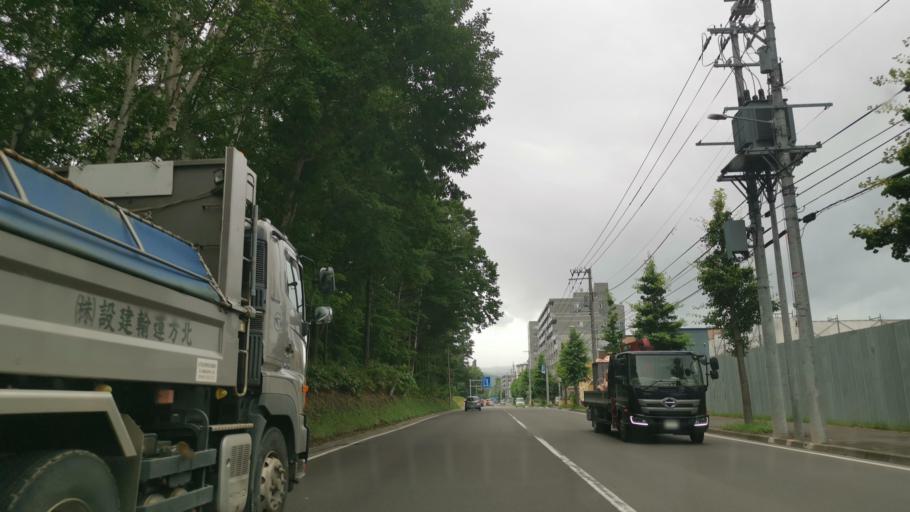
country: JP
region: Hokkaido
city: Sapporo
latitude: 42.9828
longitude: 141.3552
